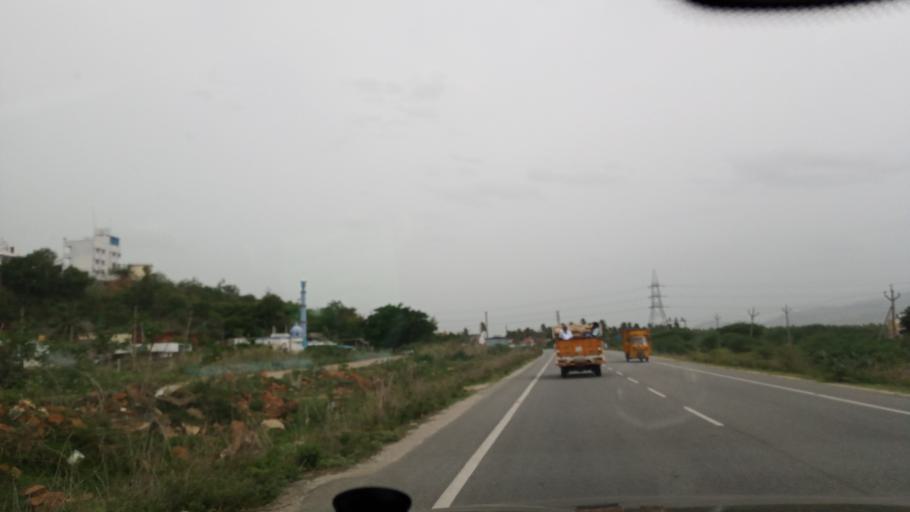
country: IN
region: Andhra Pradesh
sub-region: Chittoor
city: Nagari
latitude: 13.3453
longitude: 79.5765
